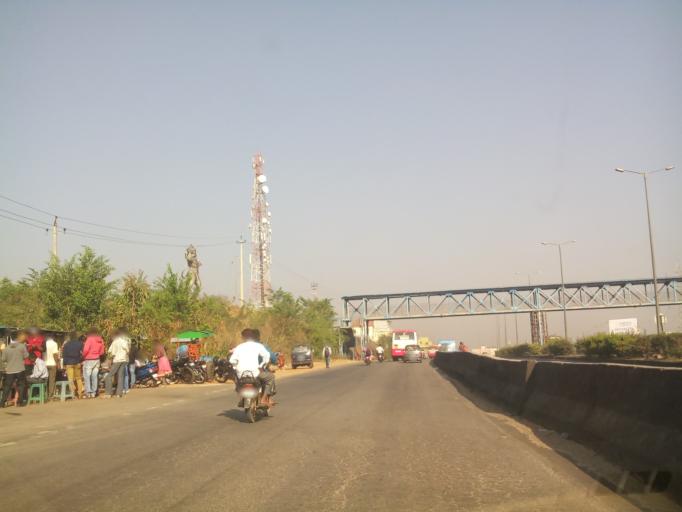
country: IN
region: Karnataka
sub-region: Bangalore Rural
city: Nelamangala
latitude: 13.0946
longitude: 77.3894
